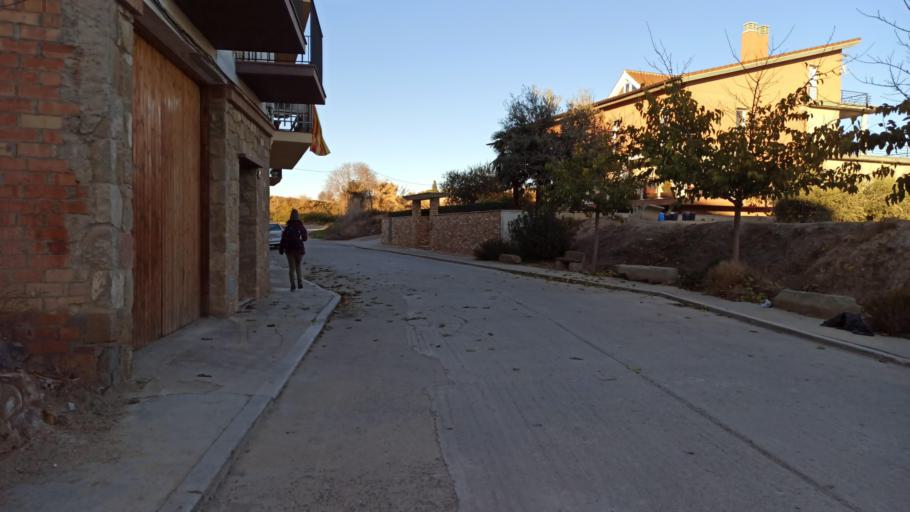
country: ES
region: Catalonia
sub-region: Provincia de Lleida
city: Penelles
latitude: 41.7591
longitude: 0.9666
